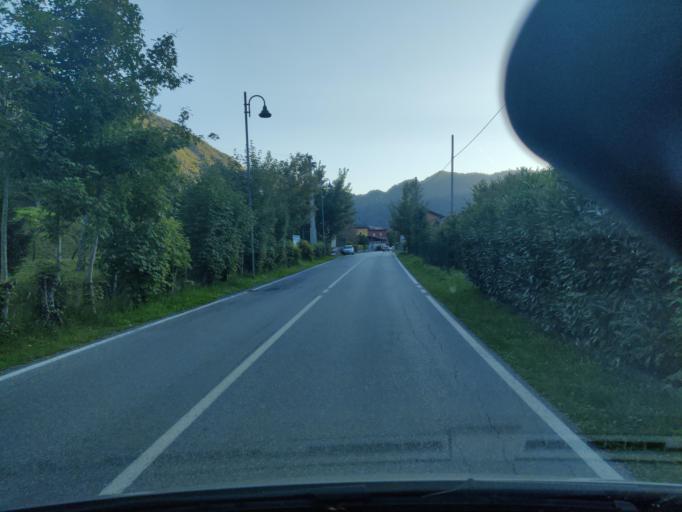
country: IT
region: Lombardy
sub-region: Provincia di Brescia
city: Crone
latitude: 45.7431
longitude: 10.4835
